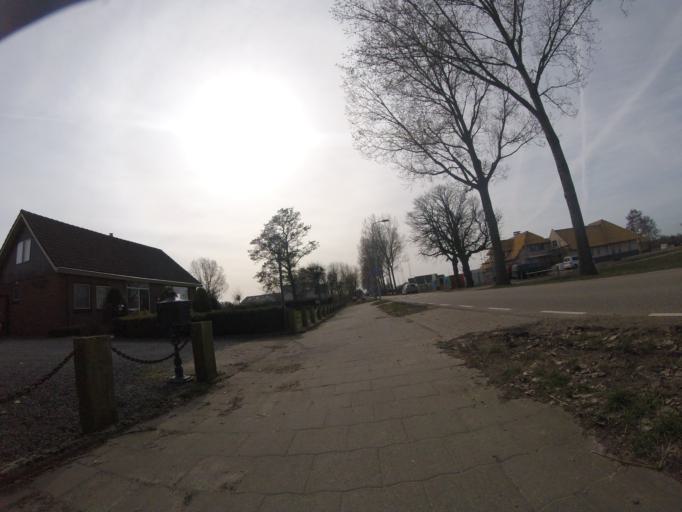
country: NL
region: North Holland
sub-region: Gemeente Bloemendaal
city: Bennebroek
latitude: 52.3149
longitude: 4.6269
